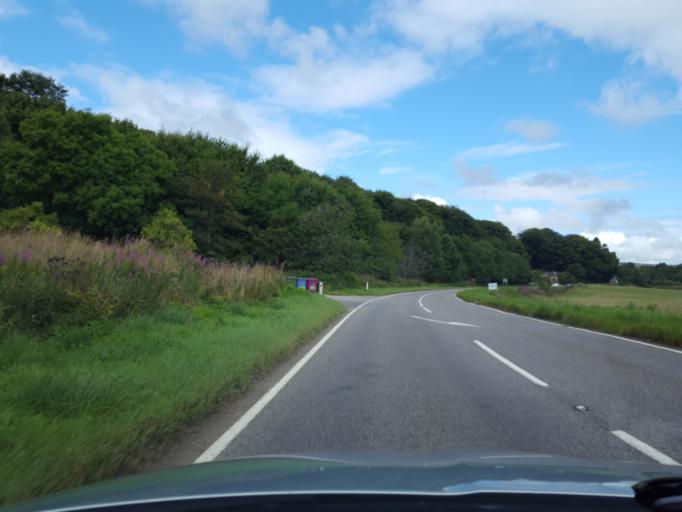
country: GB
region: Scotland
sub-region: Moray
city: Rothes
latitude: 57.5149
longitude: -3.2071
